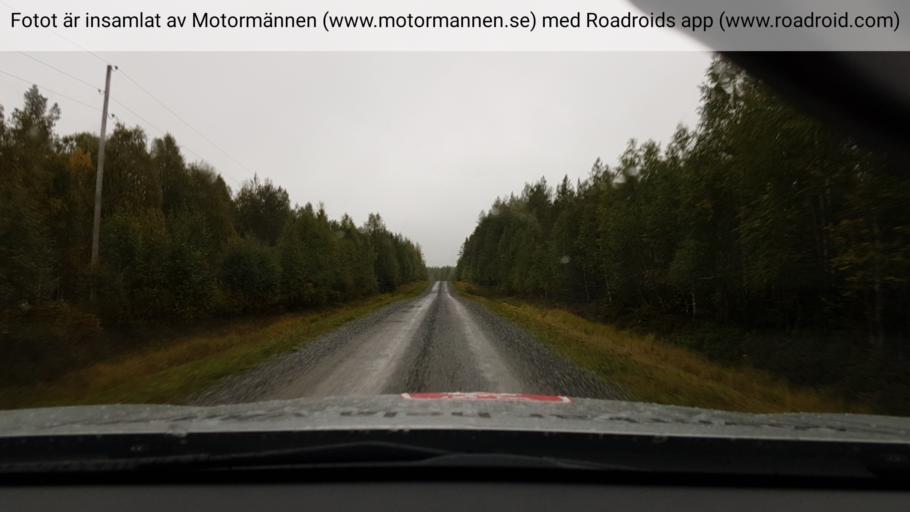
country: SE
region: Vaesterbotten
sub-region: Skelleftea Kommun
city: Storvik
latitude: 65.0364
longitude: 20.7476
